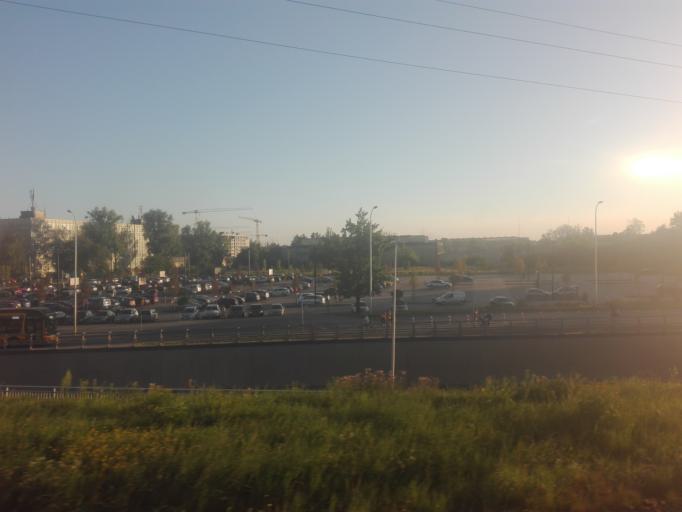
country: PL
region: Masovian Voivodeship
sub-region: Warszawa
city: Ursus
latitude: 52.2041
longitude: 20.8936
